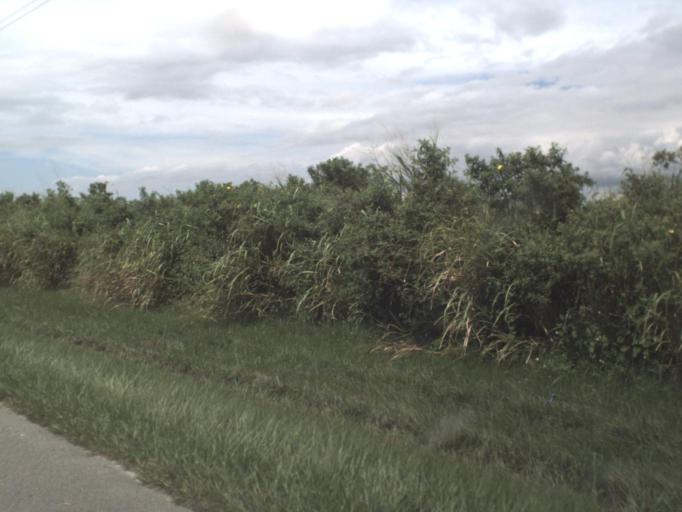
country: US
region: Florida
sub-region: Hillsborough County
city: Wimauma
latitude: 27.5924
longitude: -82.2585
